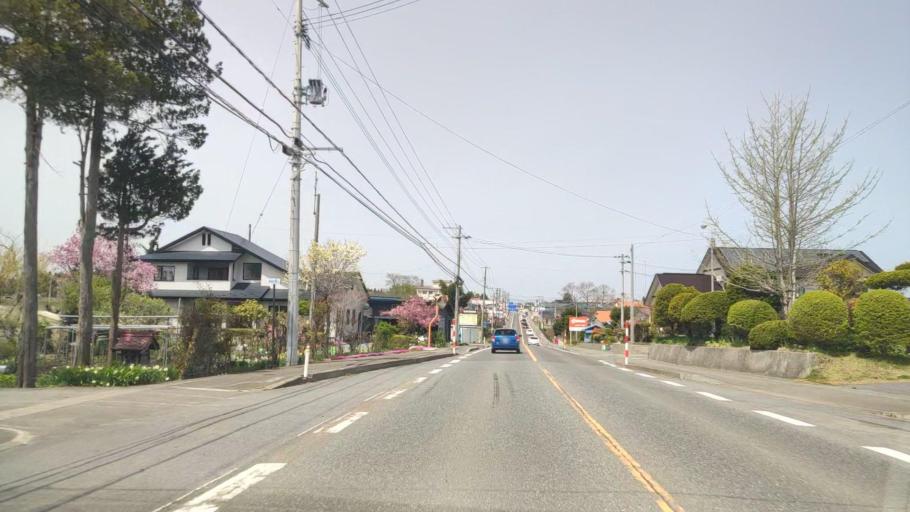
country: JP
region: Aomori
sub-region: Misawa Shi
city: Inuotose
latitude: 40.6543
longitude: 141.1939
